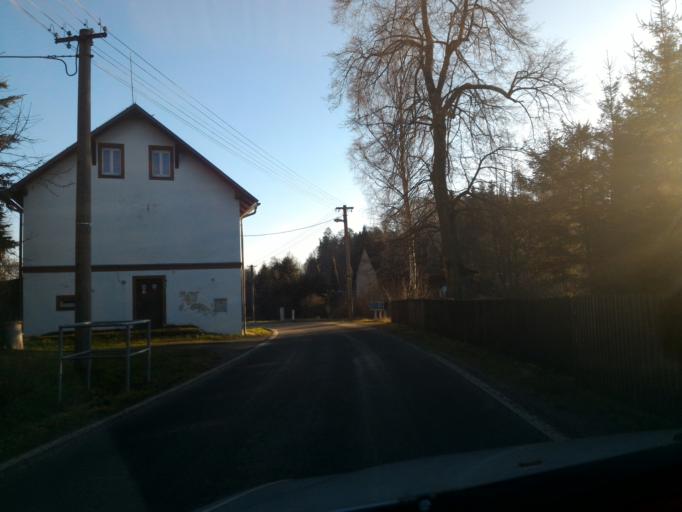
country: DE
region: Saxony
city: Kurort Oybin
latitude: 50.7983
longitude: 14.7196
